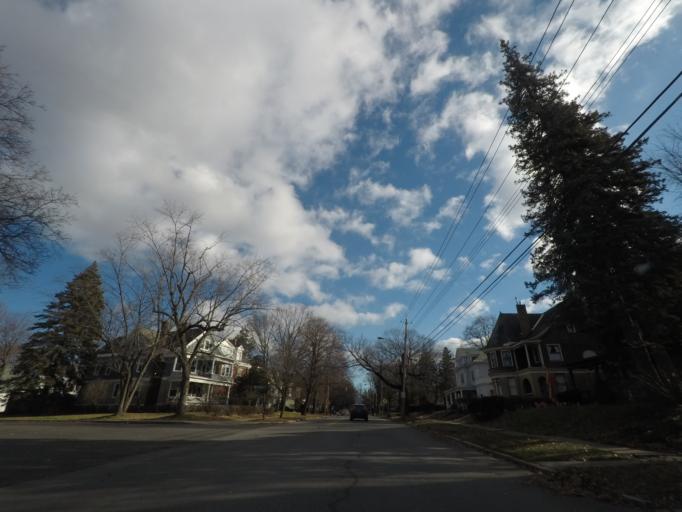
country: US
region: New York
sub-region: Schenectady County
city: Schenectady
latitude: 42.8111
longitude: -73.9217
